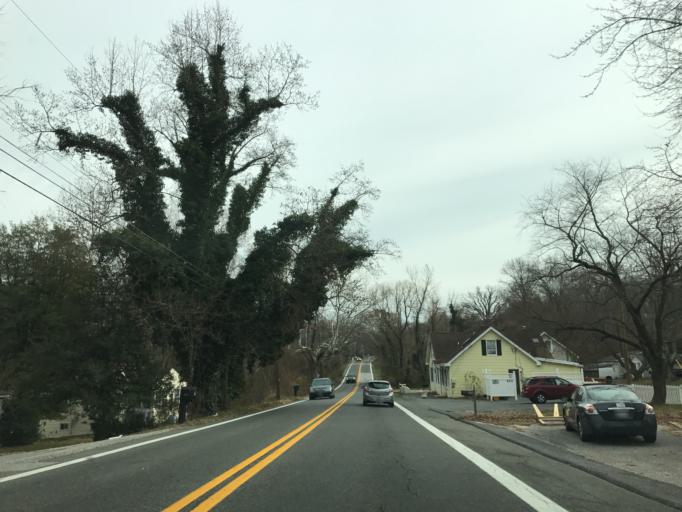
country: US
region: Maryland
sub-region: Anne Arundel County
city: Severna Park
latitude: 39.0598
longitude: -76.5336
